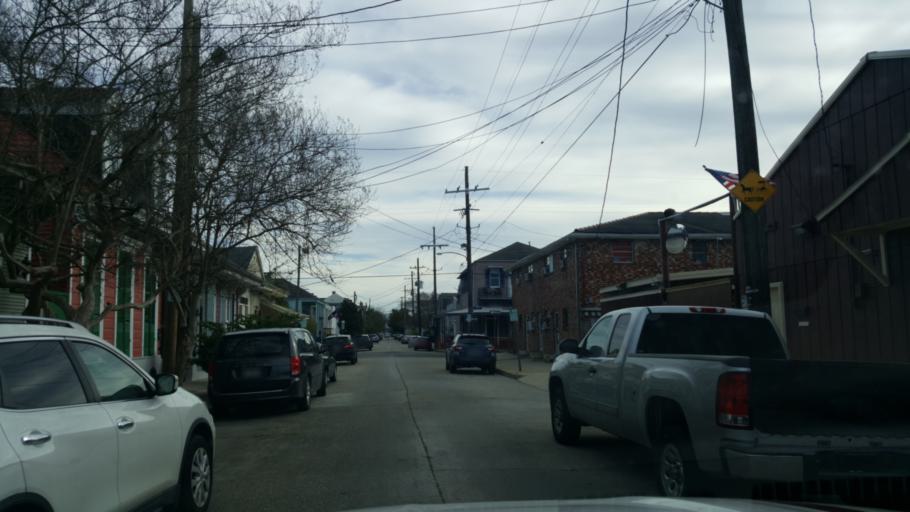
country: US
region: Louisiana
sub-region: Orleans Parish
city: New Orleans
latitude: 29.9673
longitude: -90.0610
